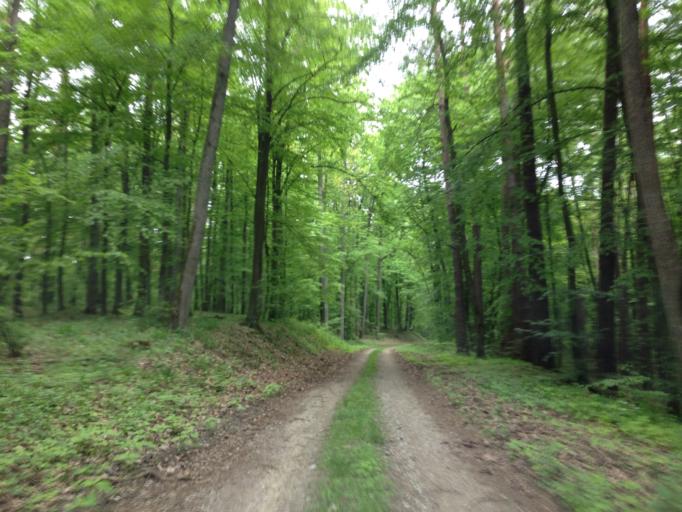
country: PL
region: Kujawsko-Pomorskie
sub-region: Powiat brodnicki
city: Gorzno
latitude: 53.2586
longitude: 19.7105
